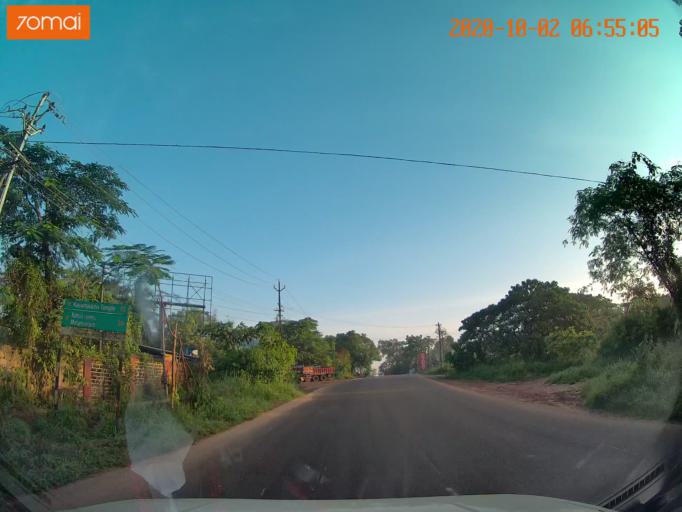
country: IN
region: Kerala
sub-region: Malappuram
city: Tirur
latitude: 10.8601
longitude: 76.0371
